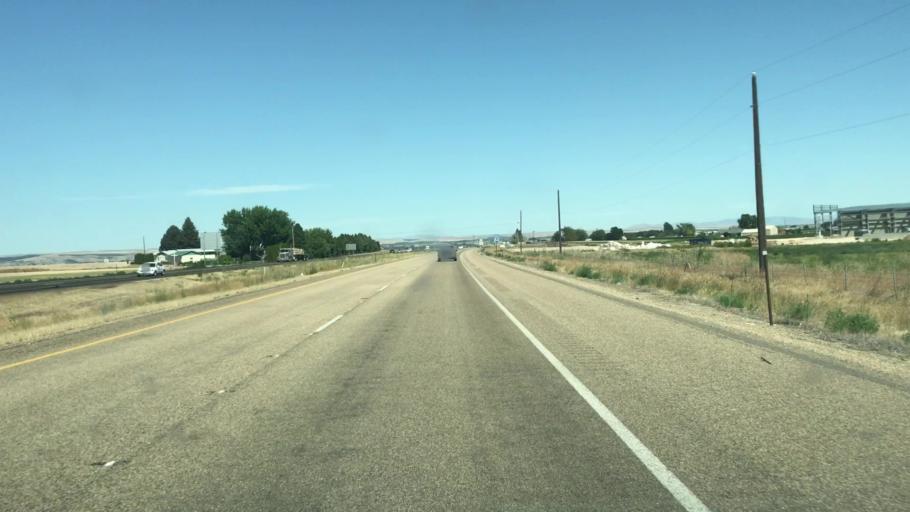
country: US
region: Idaho
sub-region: Payette County
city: Fruitland
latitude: 43.9749
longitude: -116.9182
